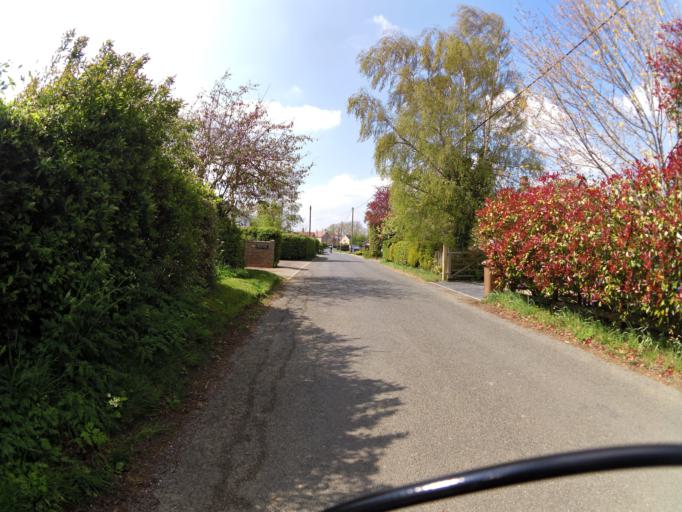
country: GB
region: England
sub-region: Suffolk
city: Hadleigh
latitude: 52.0798
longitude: 0.9907
